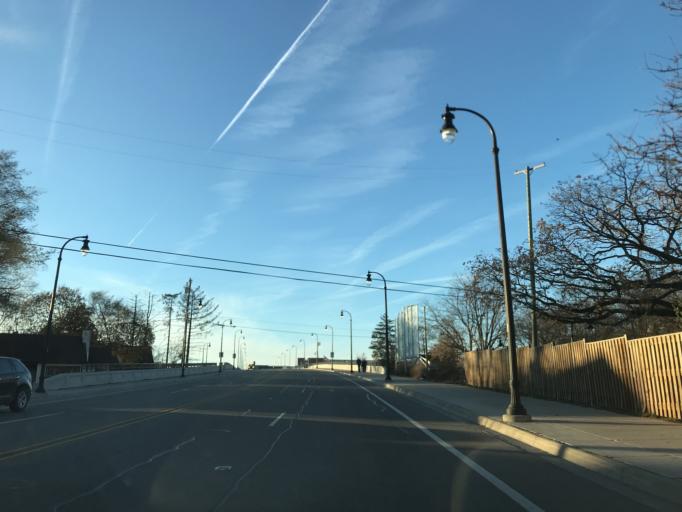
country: US
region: Michigan
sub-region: Washtenaw County
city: Ann Arbor
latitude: 42.2621
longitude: -83.7386
